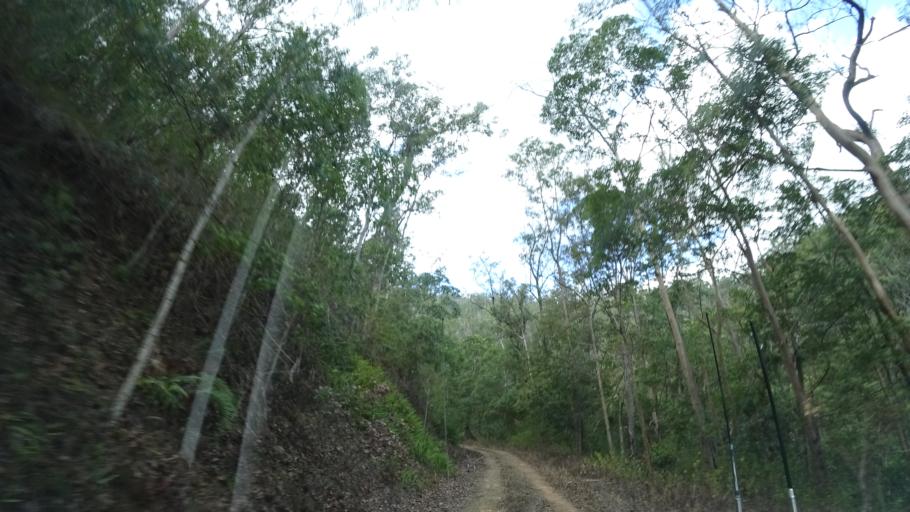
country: AU
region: Queensland
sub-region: Moreton Bay
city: Highvale
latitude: -27.3598
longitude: 152.7312
